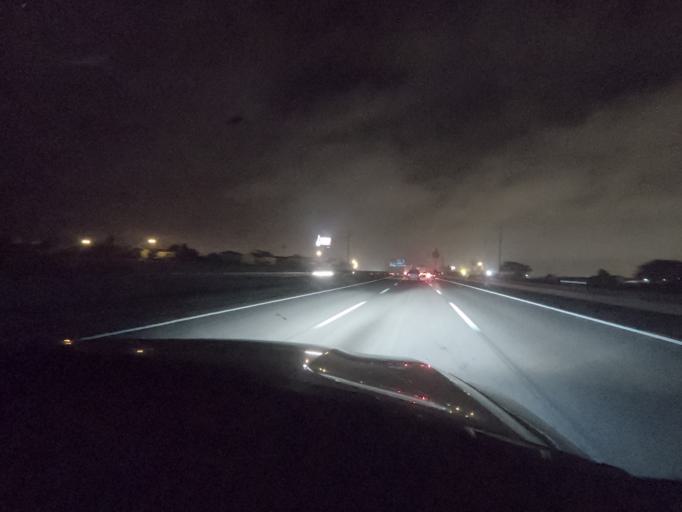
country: PT
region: Lisbon
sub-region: Alenquer
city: Carregado
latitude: 39.0357
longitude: -8.9586
